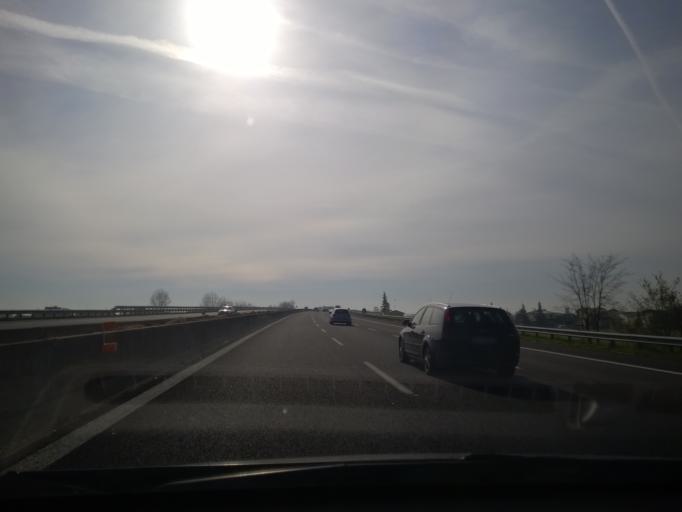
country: IT
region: Emilia-Romagna
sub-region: Provincia di Ravenna
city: Solarolo
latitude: 44.3474
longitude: 11.8362
